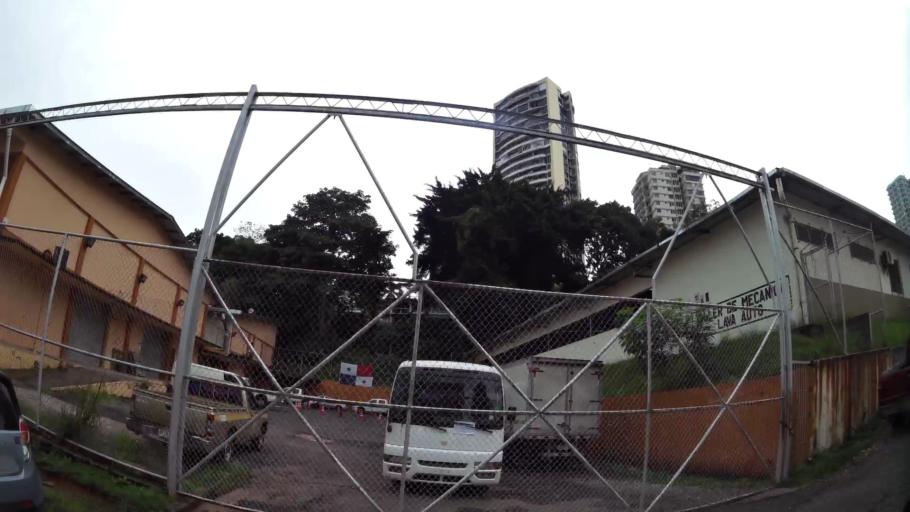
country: PA
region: Panama
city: Panama
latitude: 8.9823
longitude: -79.5312
